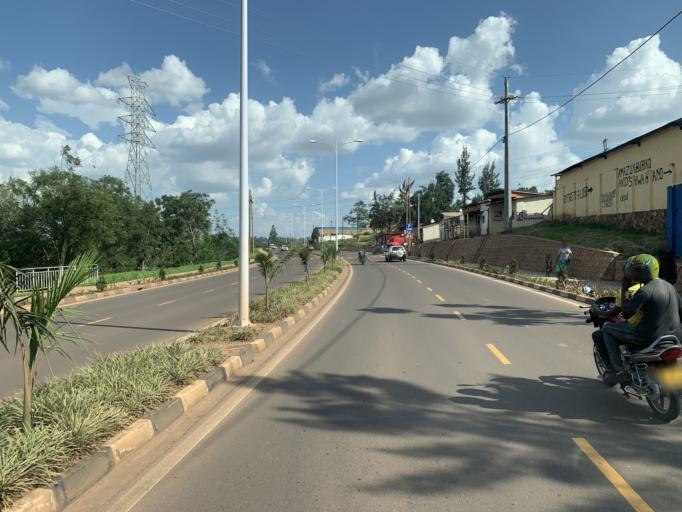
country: RW
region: Kigali
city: Kigali
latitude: -1.9633
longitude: 30.0781
